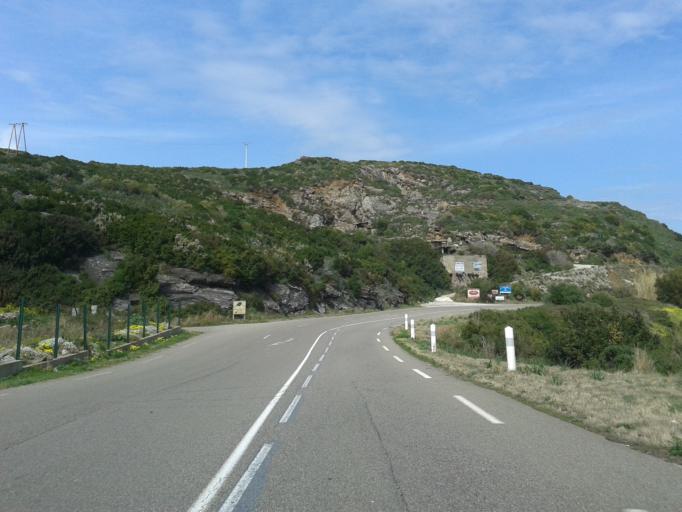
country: FR
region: Corsica
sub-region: Departement de la Haute-Corse
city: Brando
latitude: 42.8041
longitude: 9.4911
